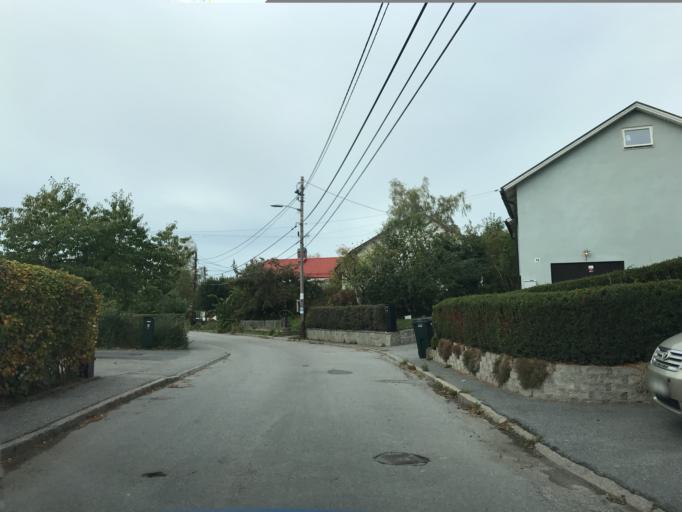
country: SE
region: Stockholm
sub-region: Huddinge Kommun
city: Segeltorp
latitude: 59.2759
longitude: 17.9671
